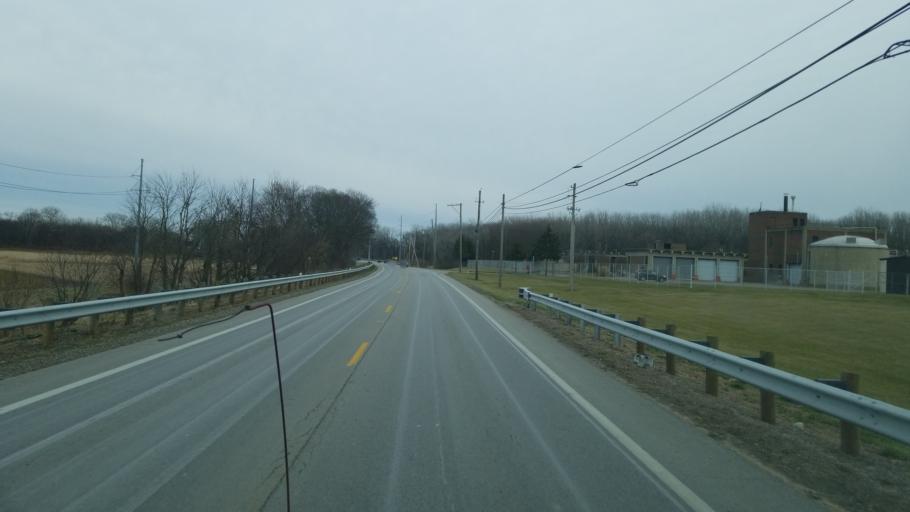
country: US
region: Ohio
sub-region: Pickaway County
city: Circleville
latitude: 39.6008
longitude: -82.9625
